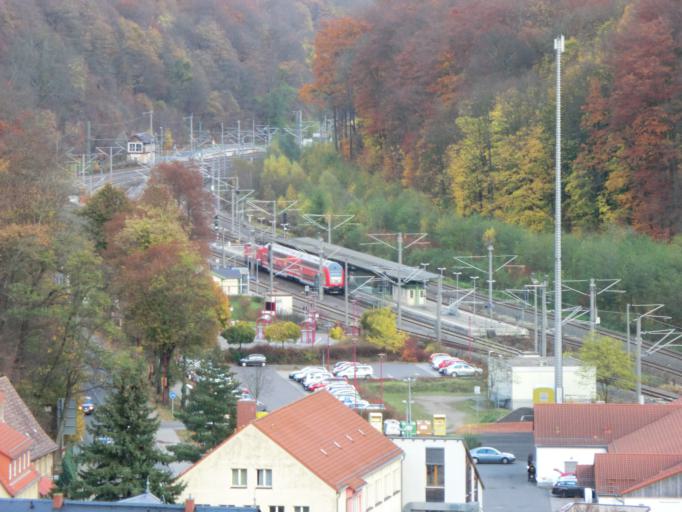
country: DE
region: Saxony
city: Tharandt
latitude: 50.9828
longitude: 13.5817
